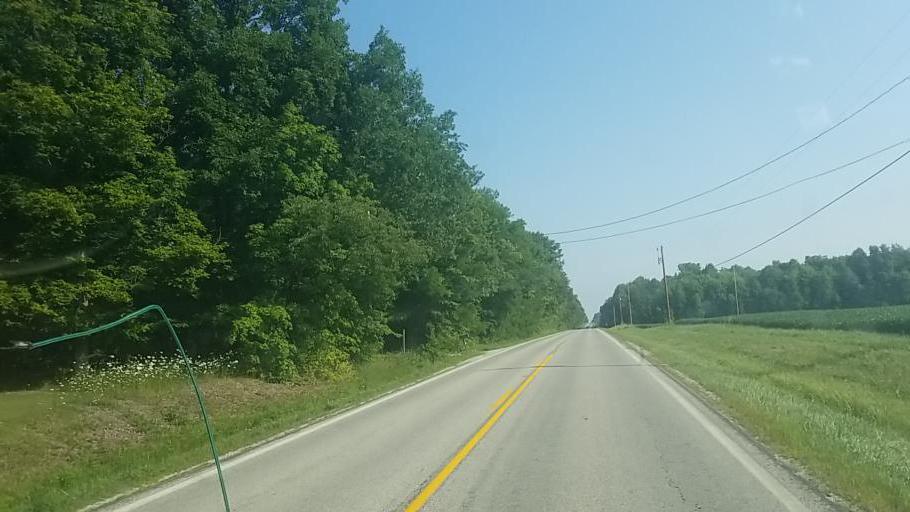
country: US
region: Ohio
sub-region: Crawford County
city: Galion
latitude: 40.6557
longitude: -82.7657
